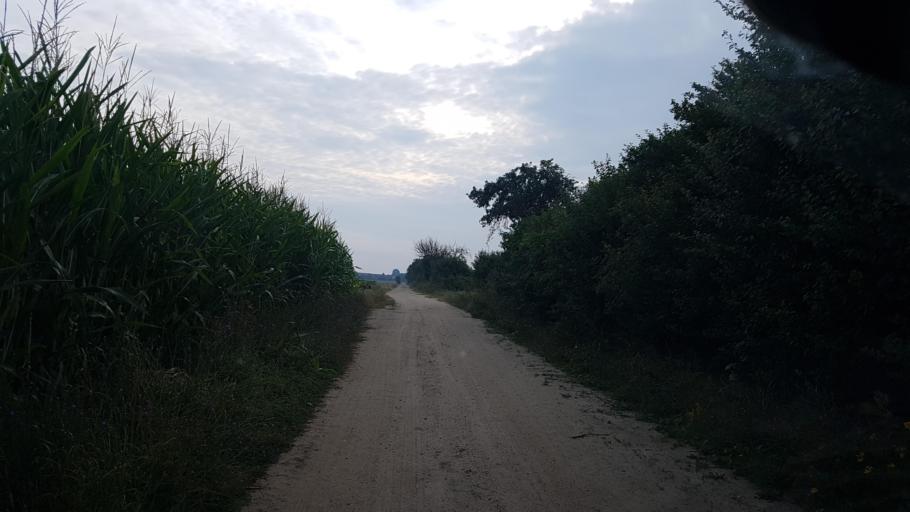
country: DE
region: Brandenburg
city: Schonborn
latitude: 51.6836
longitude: 13.4960
